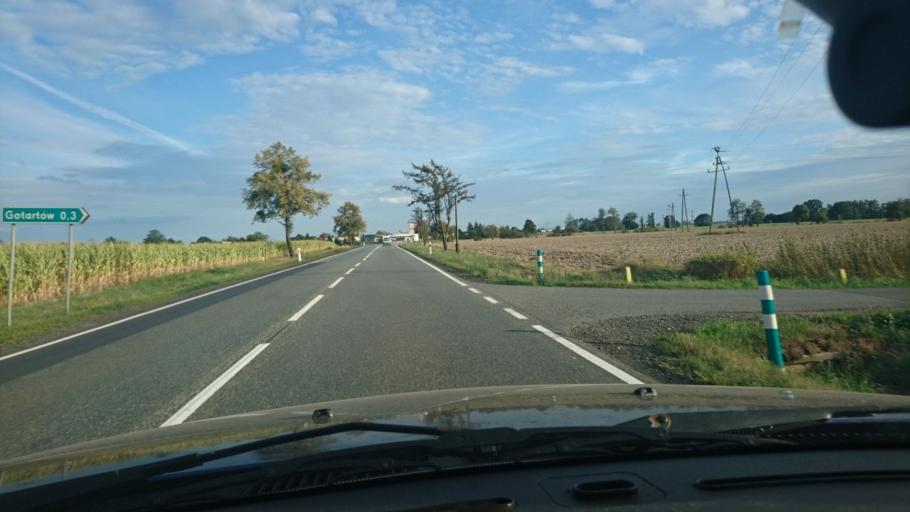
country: PL
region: Opole Voivodeship
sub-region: Powiat kluczborski
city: Kluczbork
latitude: 51.0120
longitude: 18.2028
